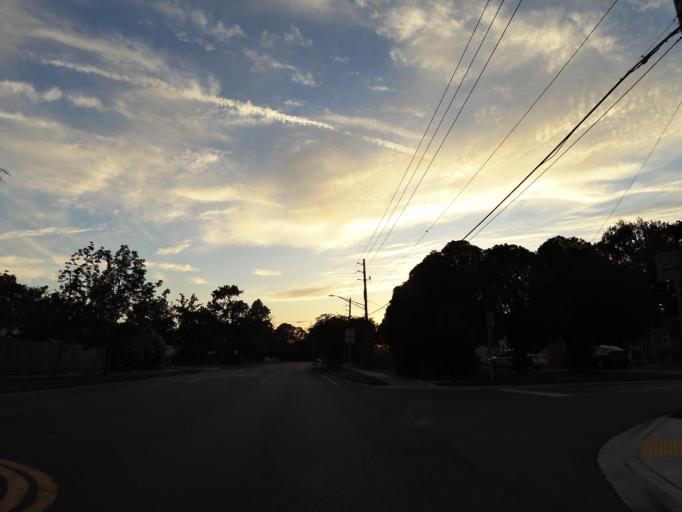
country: US
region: Florida
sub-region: Duval County
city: Jacksonville
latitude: 30.2704
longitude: -81.6033
